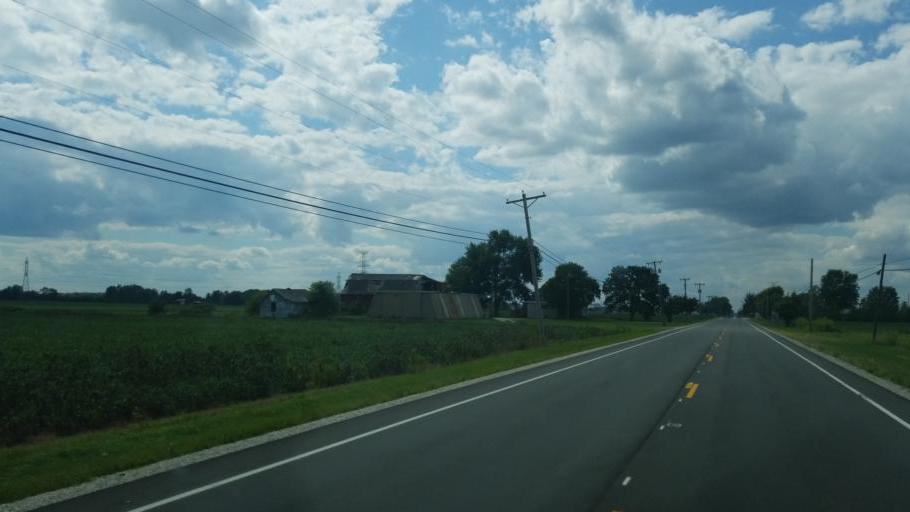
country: US
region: Ohio
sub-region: Lucas County
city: Curtice
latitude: 41.6386
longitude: -83.3238
